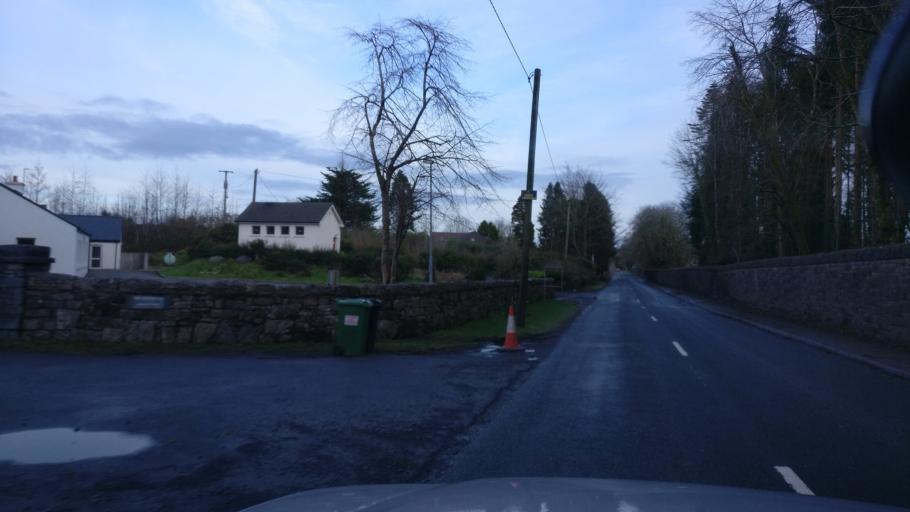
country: IE
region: Connaught
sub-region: Maigh Eo
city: Ballinrobe
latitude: 53.5426
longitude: -9.2741
